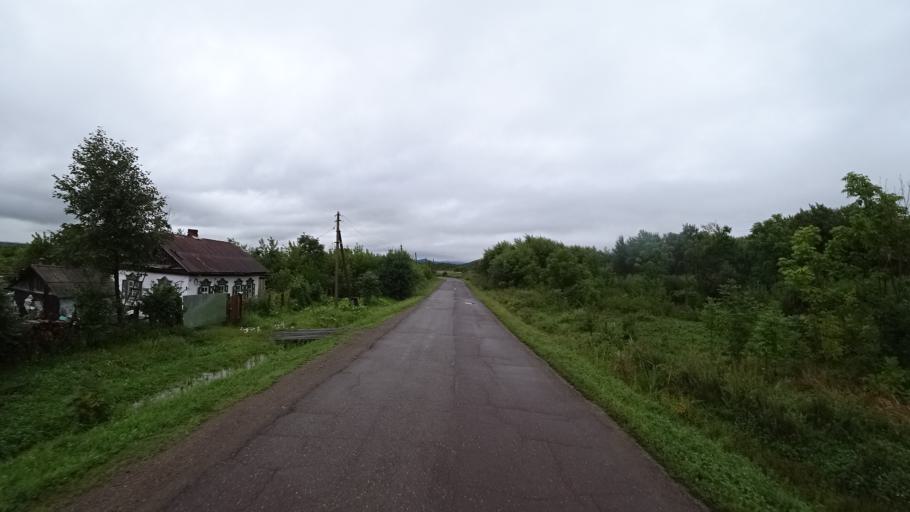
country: RU
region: Primorskiy
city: Monastyrishche
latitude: 44.2714
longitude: 132.4225
